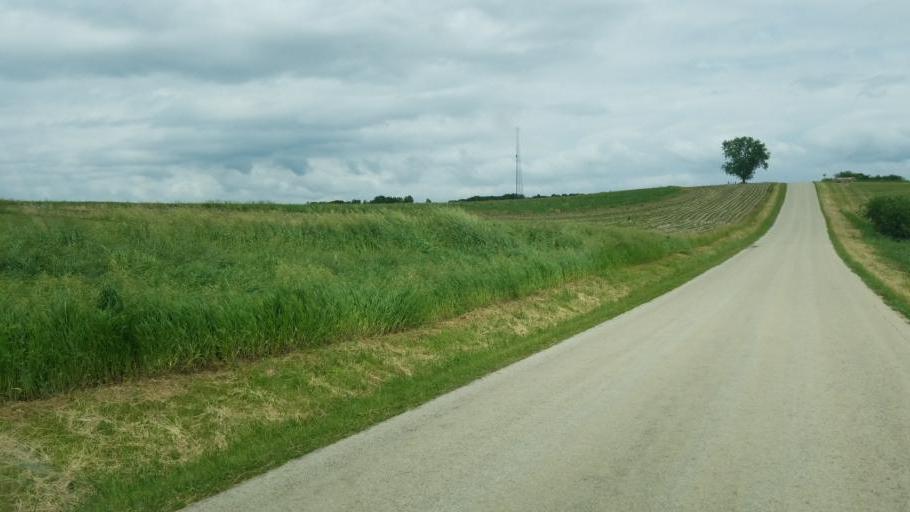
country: US
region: Wisconsin
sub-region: Monroe County
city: Cashton
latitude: 43.7112
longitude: -90.6126
